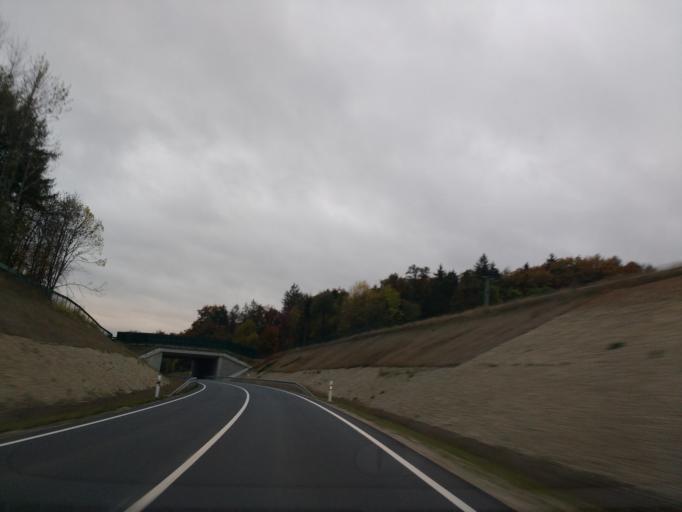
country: DE
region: Thuringia
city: Buhla
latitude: 51.4391
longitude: 10.4426
